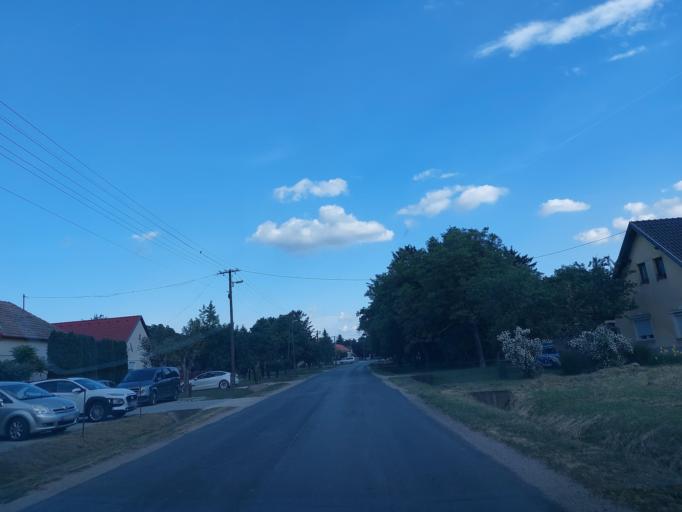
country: HU
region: Veszprem
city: Devecser
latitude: 47.1726
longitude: 17.3579
